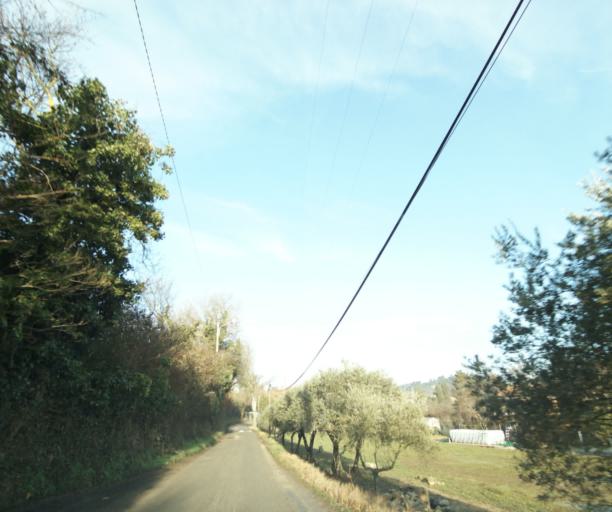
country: FR
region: Provence-Alpes-Cote d'Azur
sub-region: Departement du Var
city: Tourves
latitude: 43.4021
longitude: 5.9274
